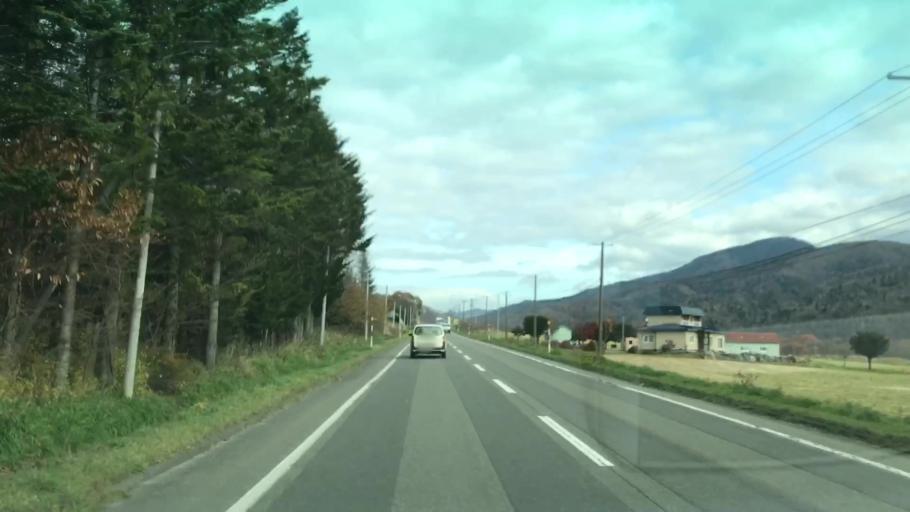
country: JP
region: Hokkaido
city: Shizunai-furukawacho
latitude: 42.7753
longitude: 142.3854
